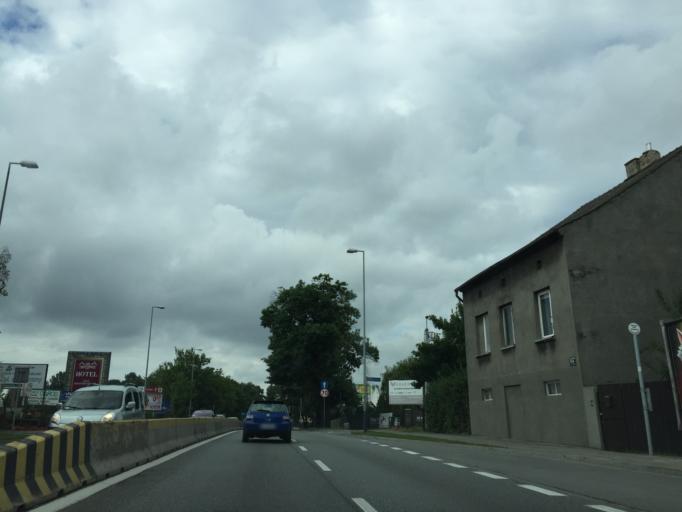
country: PL
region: Lesser Poland Voivodeship
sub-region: Powiat krakowski
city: Libertow
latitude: 50.0022
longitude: 19.9224
